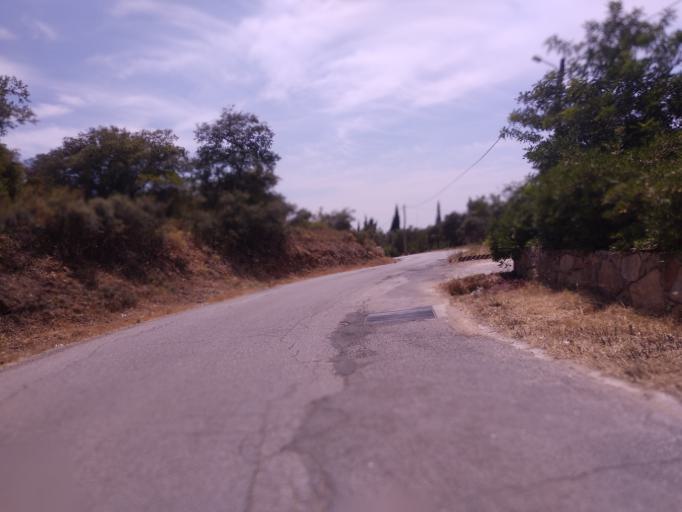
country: PT
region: Faro
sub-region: Faro
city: Santa Barbara de Nexe
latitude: 37.1097
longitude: -7.9479
